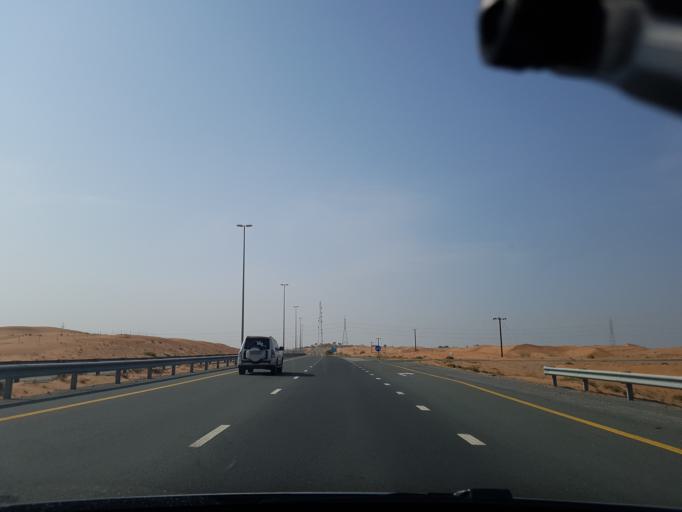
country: AE
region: Umm al Qaywayn
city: Umm al Qaywayn
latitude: 25.5239
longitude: 55.7344
